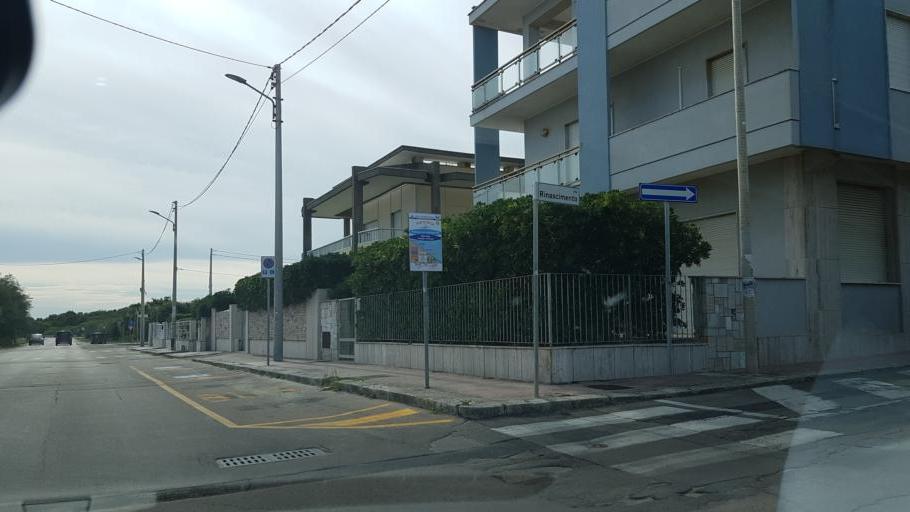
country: IT
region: Apulia
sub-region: Provincia di Lecce
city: Borgagne
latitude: 40.2990
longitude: 18.4080
